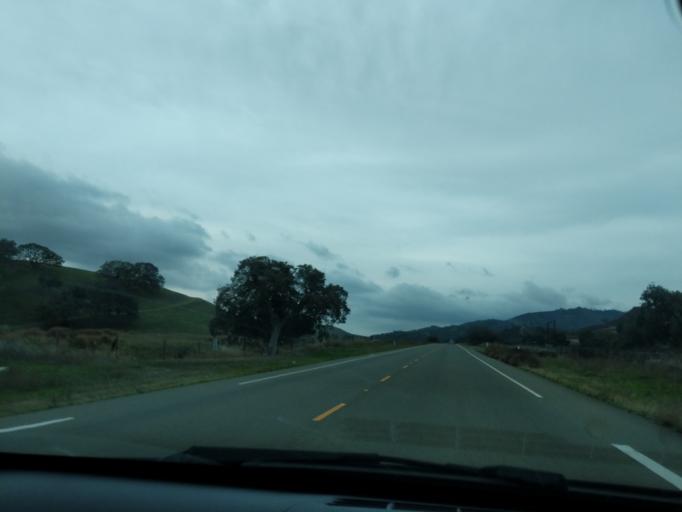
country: US
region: California
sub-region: San Benito County
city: Ridgemark
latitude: 36.6311
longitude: -121.2266
